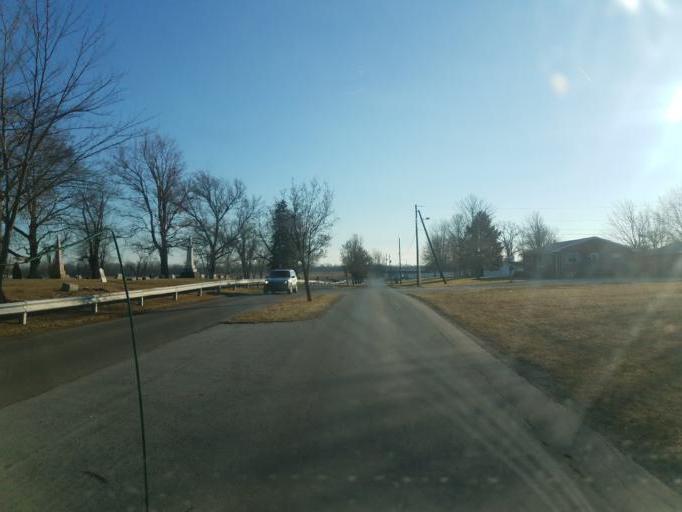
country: US
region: Ohio
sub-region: Hardin County
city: Kenton
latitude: 40.6470
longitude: -83.5905
